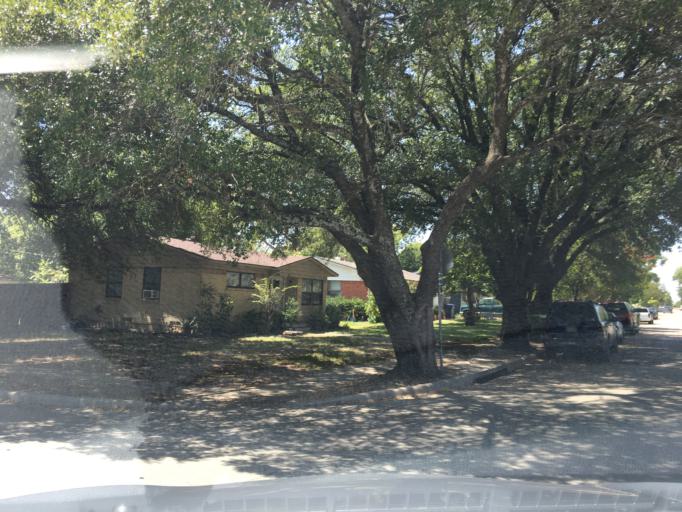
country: US
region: Texas
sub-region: Dallas County
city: Garland
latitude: 32.8933
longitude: -96.6259
